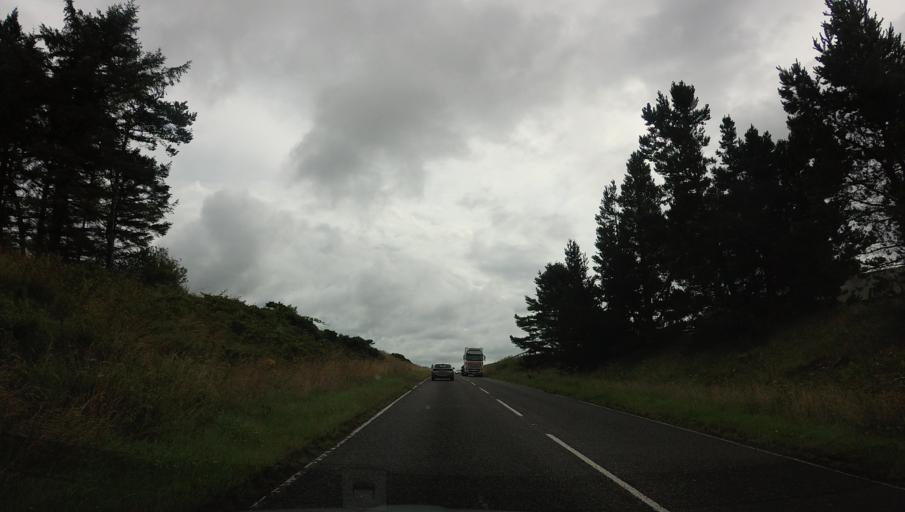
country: GB
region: Scotland
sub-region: Aberdeenshire
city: Stonehaven
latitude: 56.9474
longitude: -2.2190
